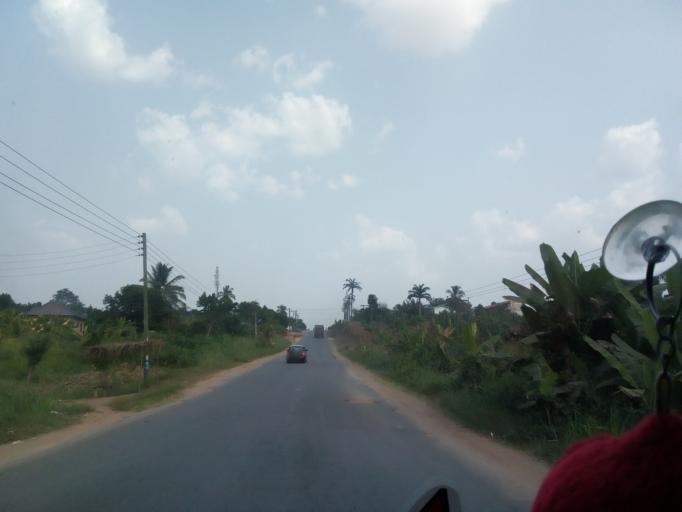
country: GH
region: Eastern
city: Suhum
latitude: 6.0415
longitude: -0.4421
